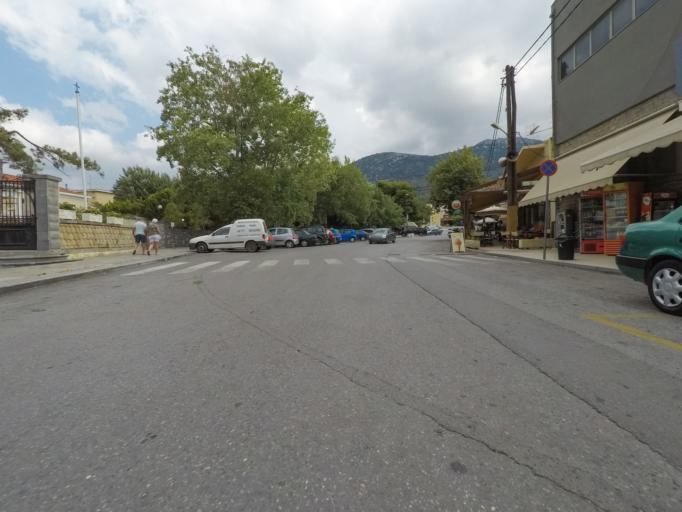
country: GR
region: Crete
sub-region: Nomos Lasithiou
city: Neapoli
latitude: 35.2569
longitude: 25.6074
